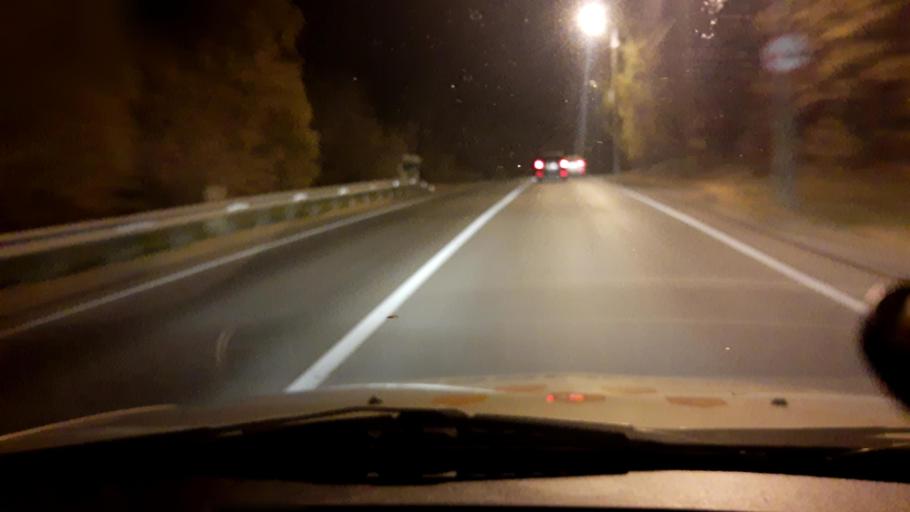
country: RU
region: Bashkortostan
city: Ufa
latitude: 54.8527
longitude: 56.0743
